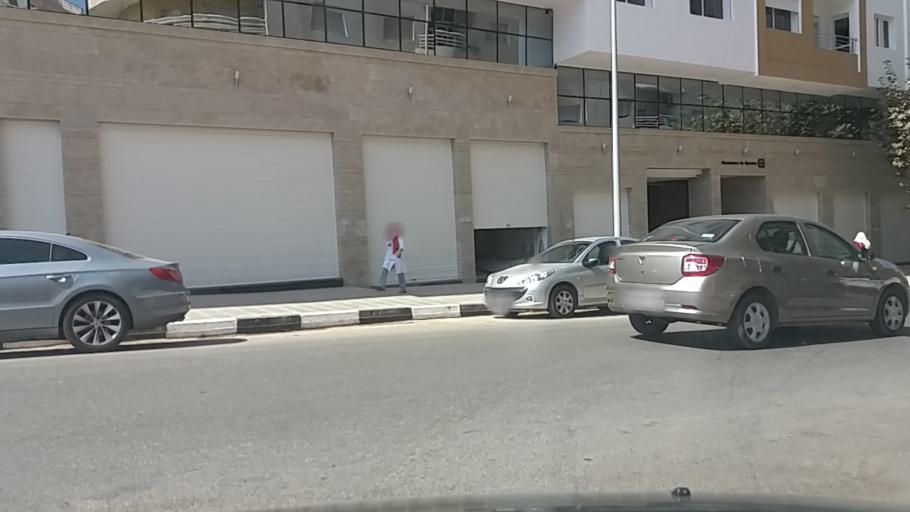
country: MA
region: Gharb-Chrarda-Beni Hssen
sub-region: Kenitra Province
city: Kenitra
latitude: 34.2567
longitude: -6.5819
